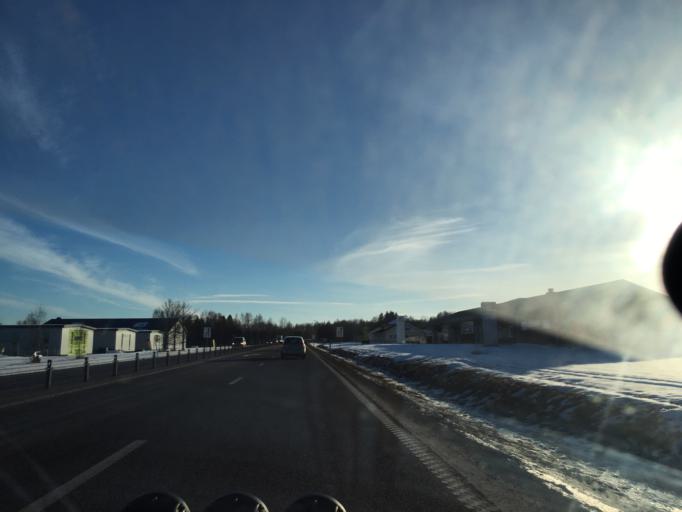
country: SE
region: Dalarna
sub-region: Borlange Kommun
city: Borlaenge
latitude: 60.4701
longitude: 15.4000
